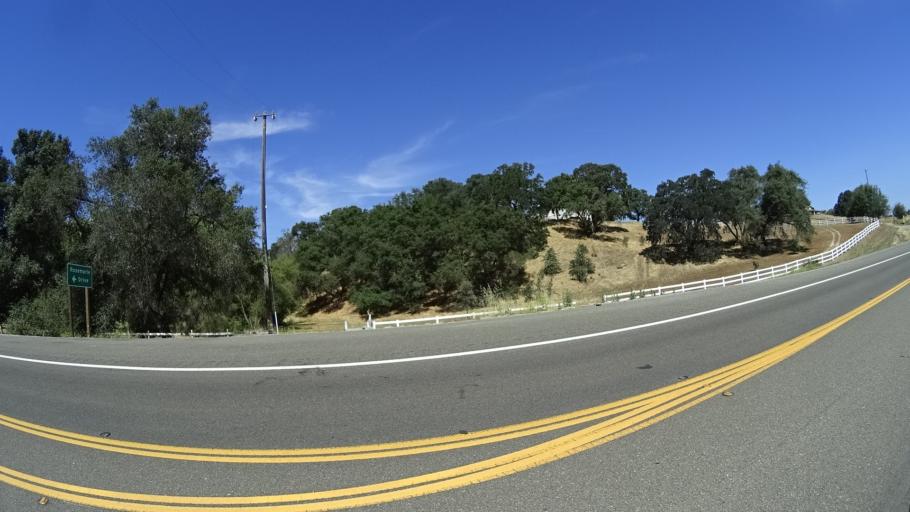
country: US
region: California
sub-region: Calaveras County
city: Rancho Calaveras
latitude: 38.1130
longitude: -120.9084
